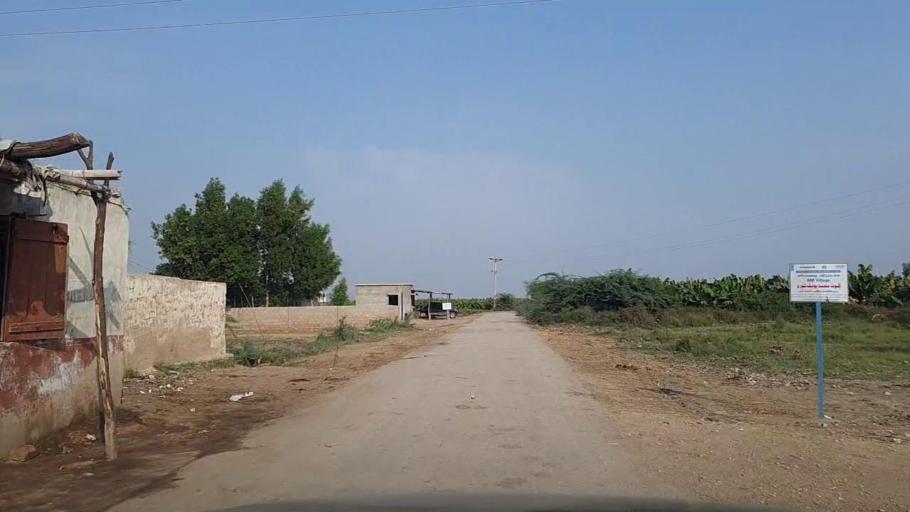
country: PK
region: Sindh
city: Thatta
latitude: 24.6459
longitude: 67.9344
